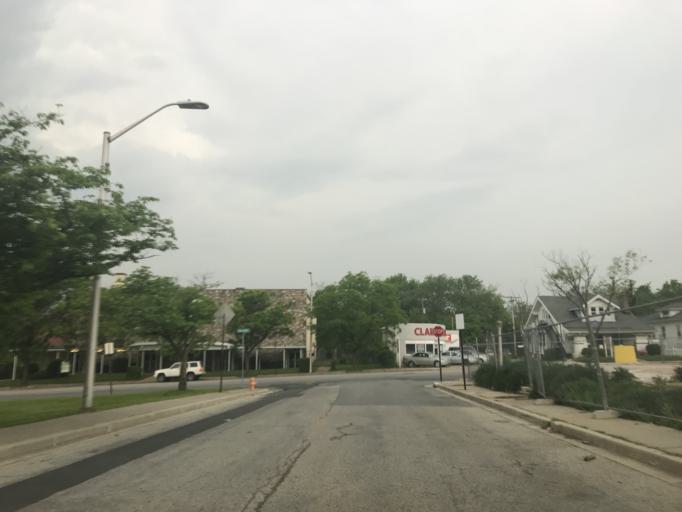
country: US
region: Maryland
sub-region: Baltimore County
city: Parkville
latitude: 39.3556
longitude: -76.5579
